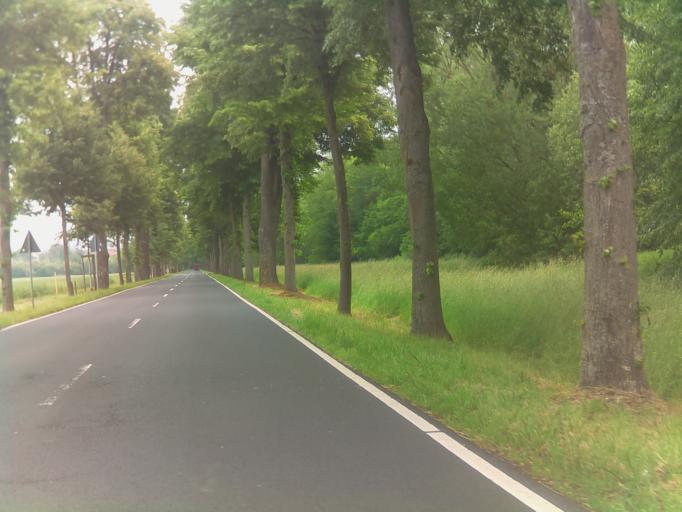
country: DE
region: Hesse
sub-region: Regierungsbezirk Kassel
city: Fulda
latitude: 50.5222
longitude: 9.6665
